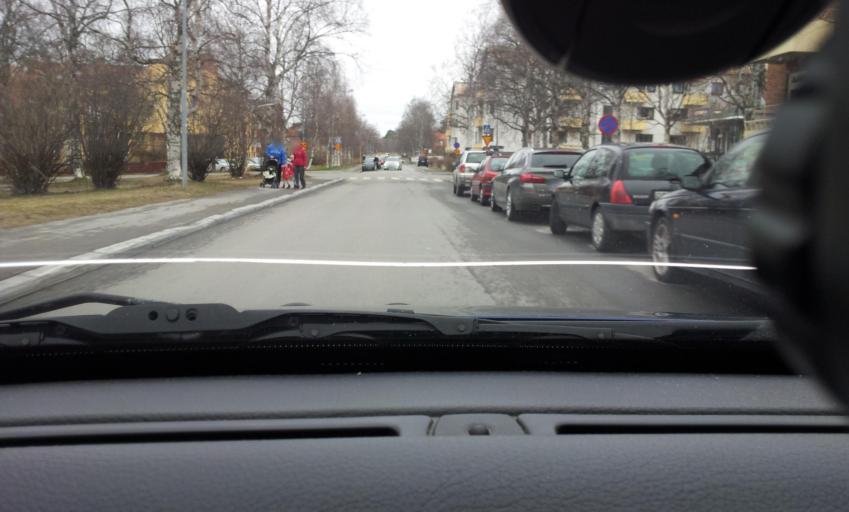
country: SE
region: Jaemtland
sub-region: OEstersunds Kommun
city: Ostersund
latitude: 63.1789
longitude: 14.6476
